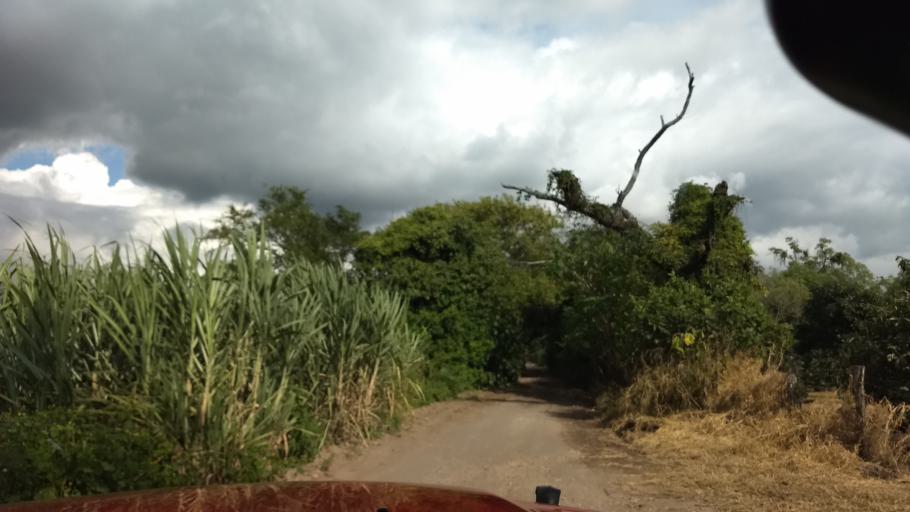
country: MX
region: Colima
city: Suchitlan
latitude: 19.4614
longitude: -103.7583
